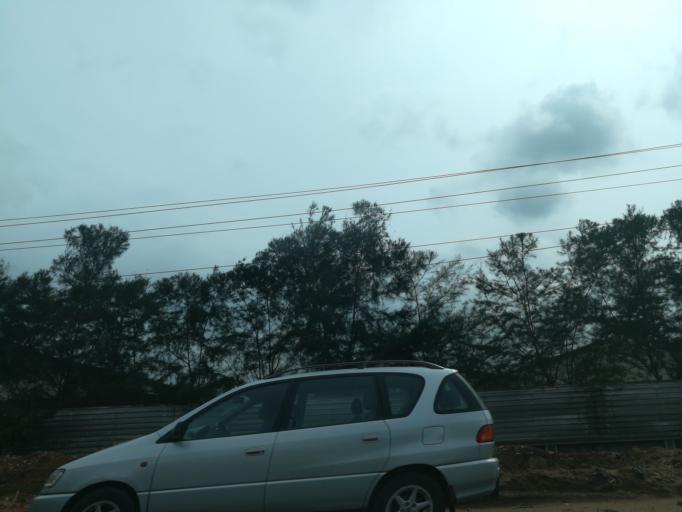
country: NG
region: Lagos
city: Ikeja
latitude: 6.6108
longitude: 3.3673
